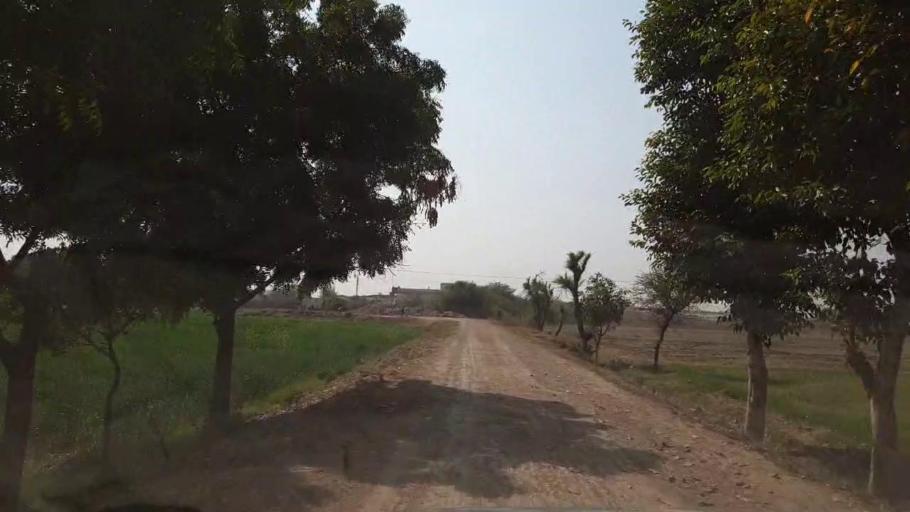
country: PK
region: Sindh
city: Mirpur Khas
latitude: 25.6438
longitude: 69.1525
